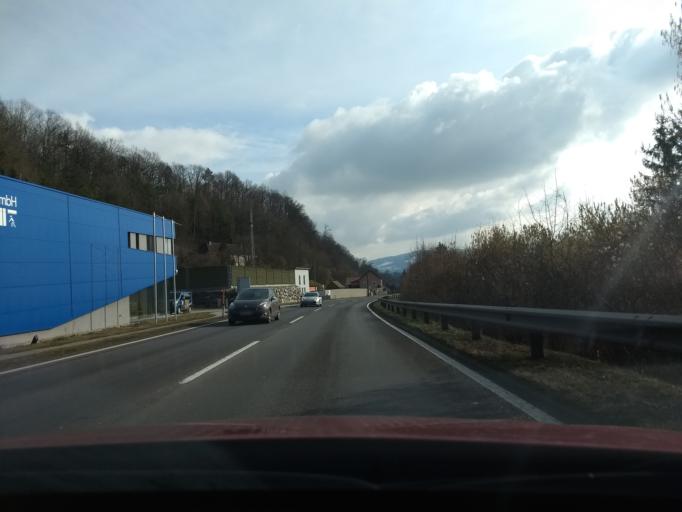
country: AT
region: Upper Austria
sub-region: Politischer Bezirk Steyr-Land
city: Garsten
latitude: 48.0501
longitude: 14.3653
